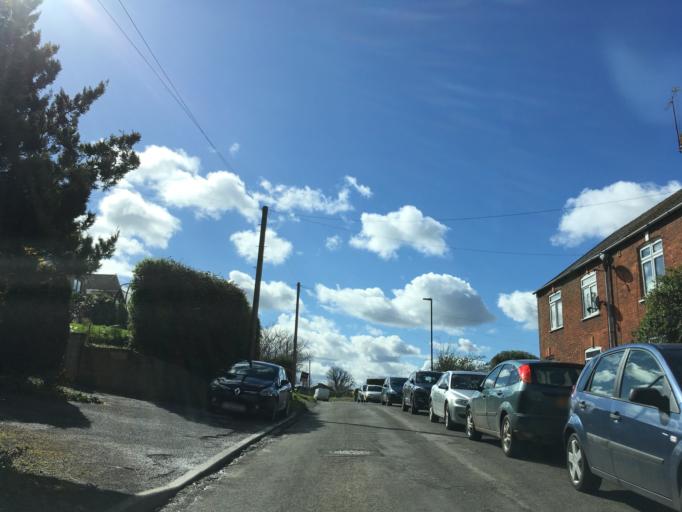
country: GB
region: England
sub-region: Gloucestershire
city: Wotton-under-Edge
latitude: 51.6331
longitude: -2.3436
